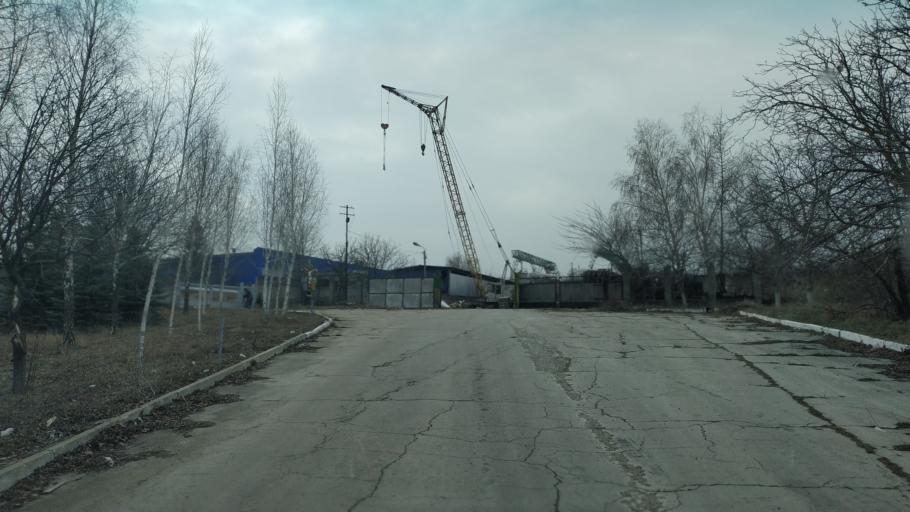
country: MD
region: Chisinau
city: Singera
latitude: 46.9124
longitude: 29.0120
